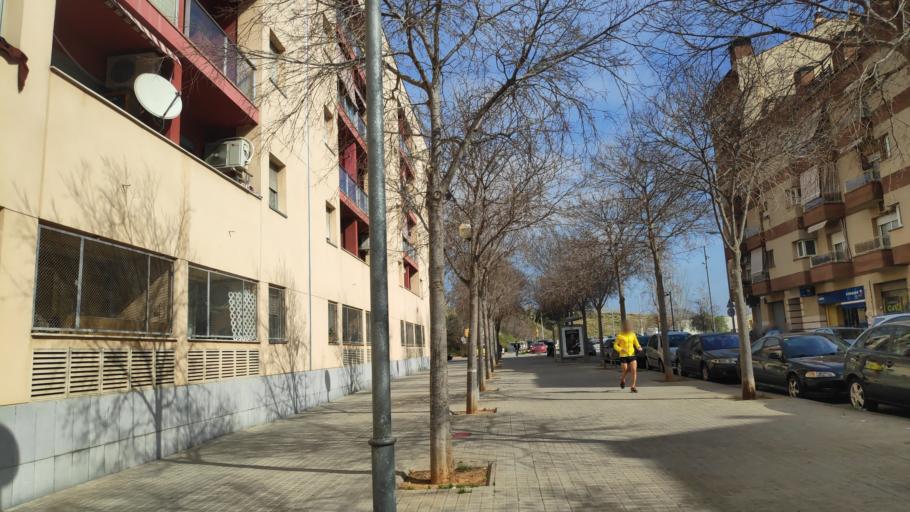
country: ES
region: Catalonia
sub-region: Provincia de Barcelona
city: Sant Quirze del Valles
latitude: 41.5581
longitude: 2.0852
